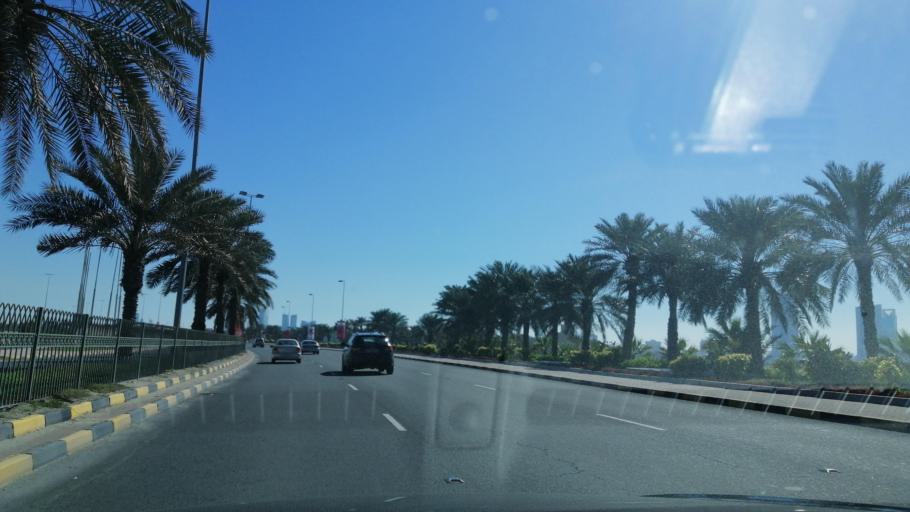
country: BH
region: Muharraq
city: Al Muharraq
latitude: 26.2555
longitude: 50.6032
